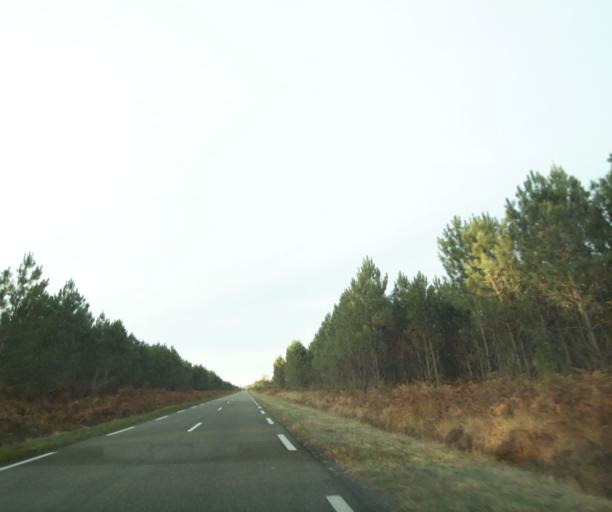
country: FR
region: Aquitaine
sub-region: Departement des Landes
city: Roquefort
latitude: 44.1797
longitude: -0.1456
